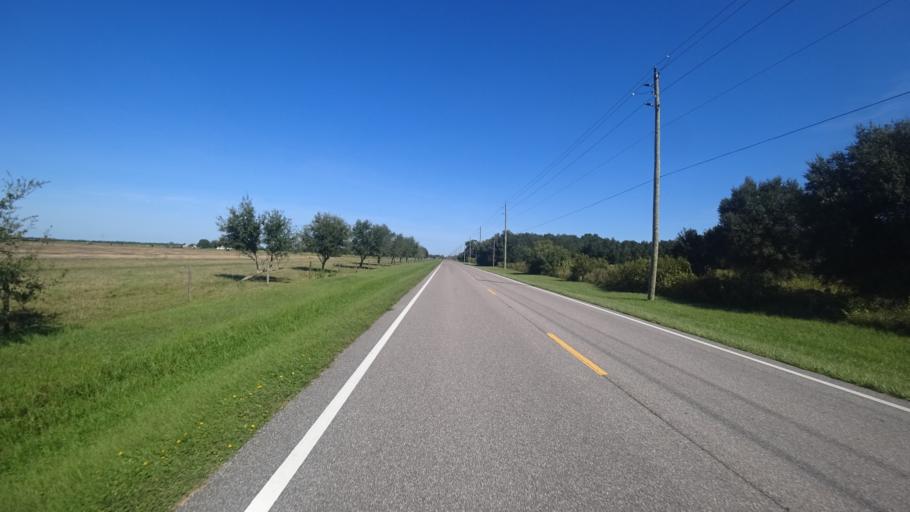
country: US
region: Florida
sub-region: Sarasota County
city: Lake Sarasota
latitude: 27.3668
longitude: -82.2684
